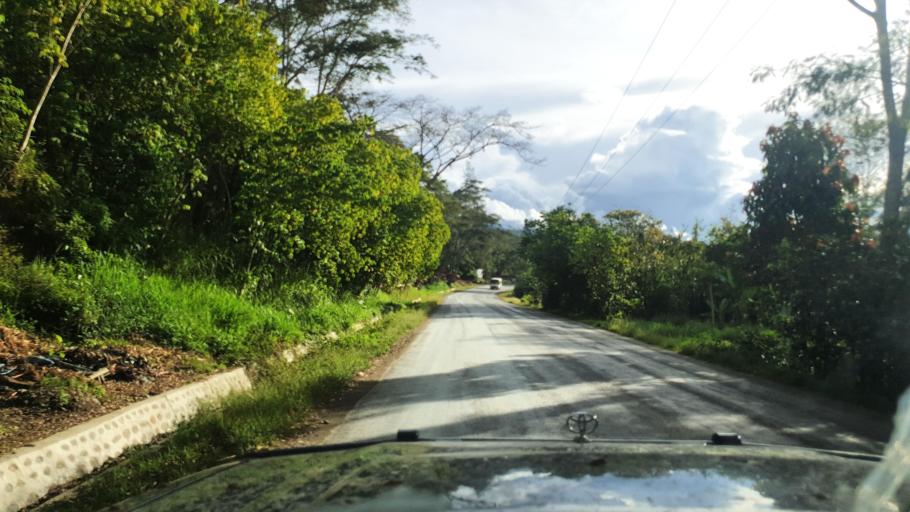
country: PG
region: Jiwaka
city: Minj
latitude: -5.8686
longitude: 144.6539
